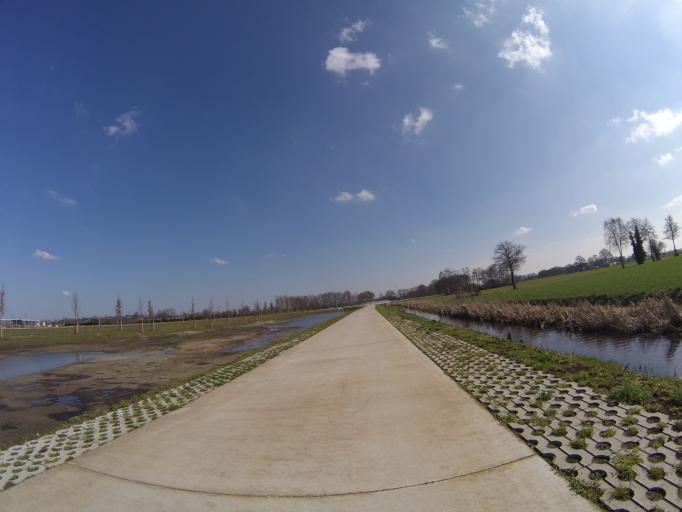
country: NL
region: Gelderland
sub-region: Gemeente Barneveld
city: Voorthuizen
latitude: 52.1576
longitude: 5.6209
